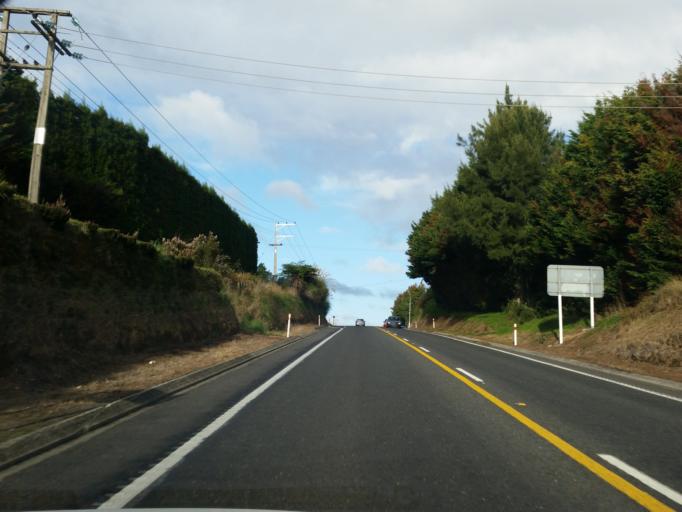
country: NZ
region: Bay of Plenty
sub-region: Western Bay of Plenty District
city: Katikati
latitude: -37.6616
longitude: 176.0091
